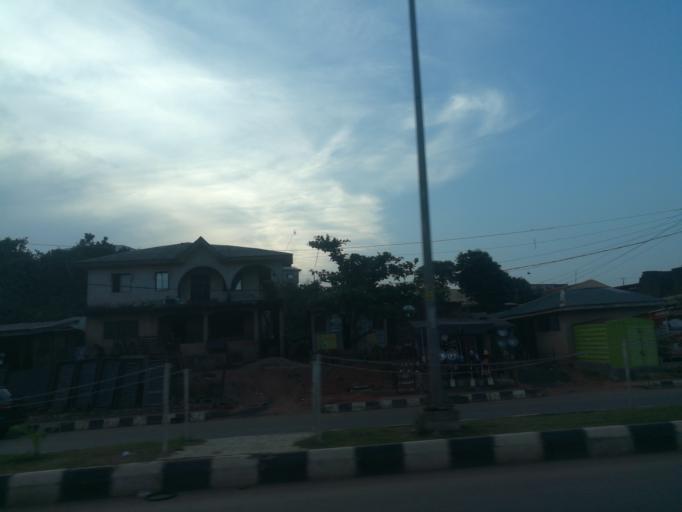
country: NG
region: Ogun
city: Abeokuta
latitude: 7.1679
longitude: 3.3726
